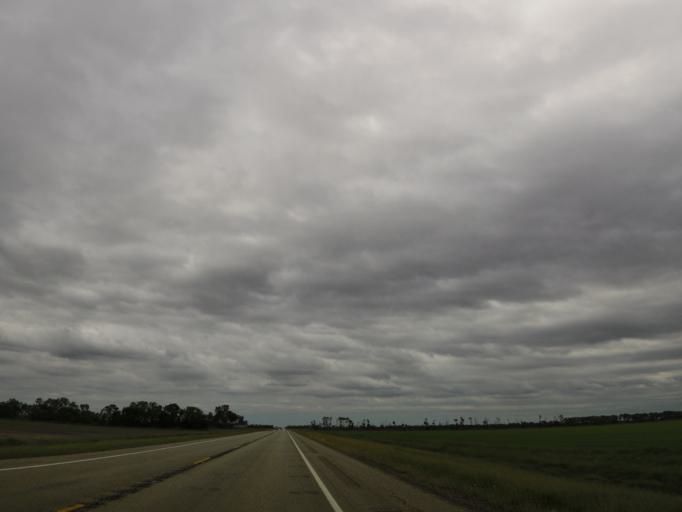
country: US
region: North Dakota
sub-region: Walsh County
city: Grafton
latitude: 48.5159
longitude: -97.4477
